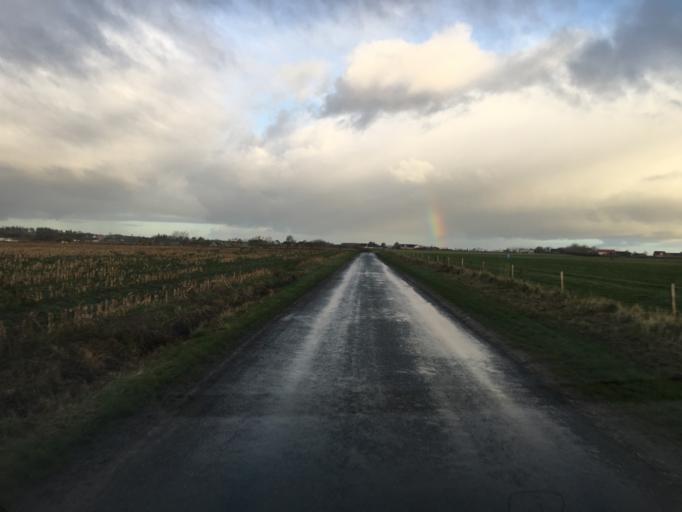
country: DK
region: South Denmark
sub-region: Tonder Kommune
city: Sherrebek
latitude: 55.1477
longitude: 8.8266
